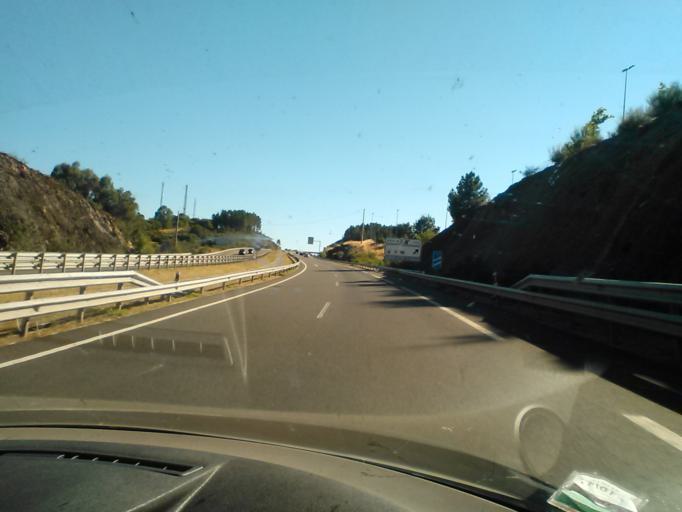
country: ES
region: Galicia
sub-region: Provincia de Ourense
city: Rios
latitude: 42.0314
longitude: -7.1787
